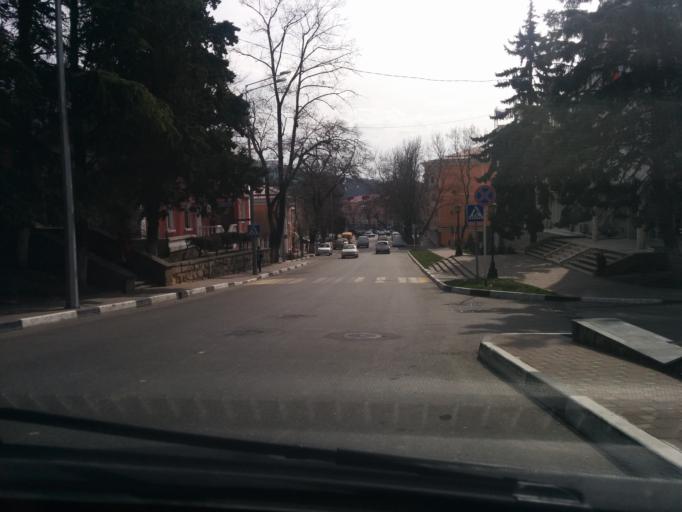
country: RU
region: Krasnodarskiy
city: Tuapse
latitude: 44.1011
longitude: 39.0783
